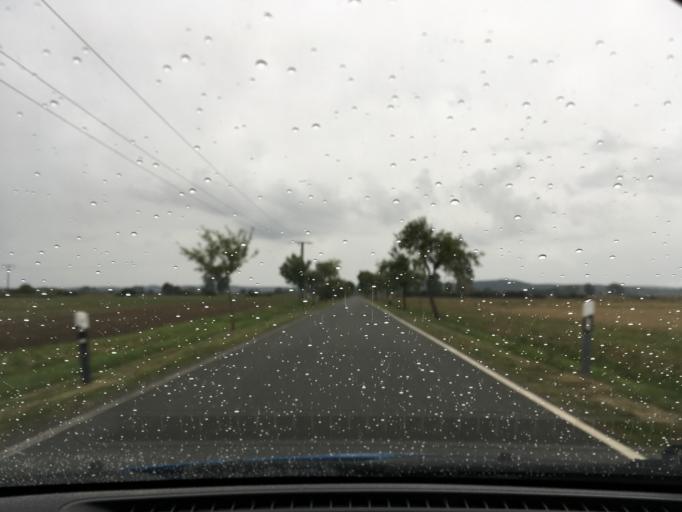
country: DE
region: Lower Saxony
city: Hitzacker
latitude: 53.2223
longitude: 10.9879
